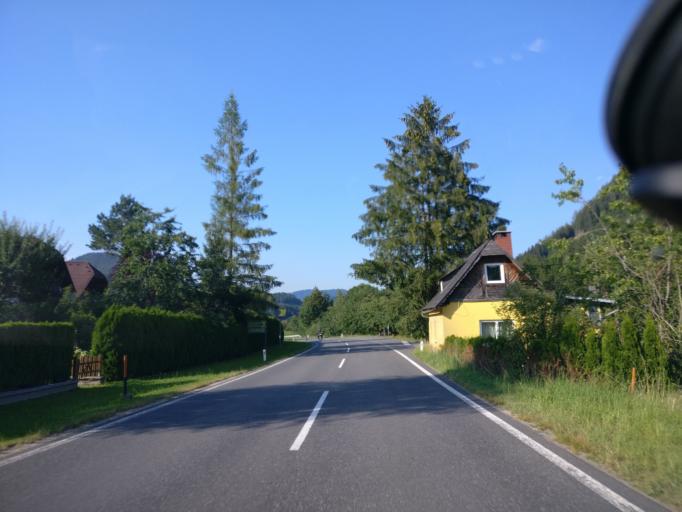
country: AT
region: Lower Austria
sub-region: Politischer Bezirk Scheibbs
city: Gostling an der Ybbs
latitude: 47.7852
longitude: 14.9153
